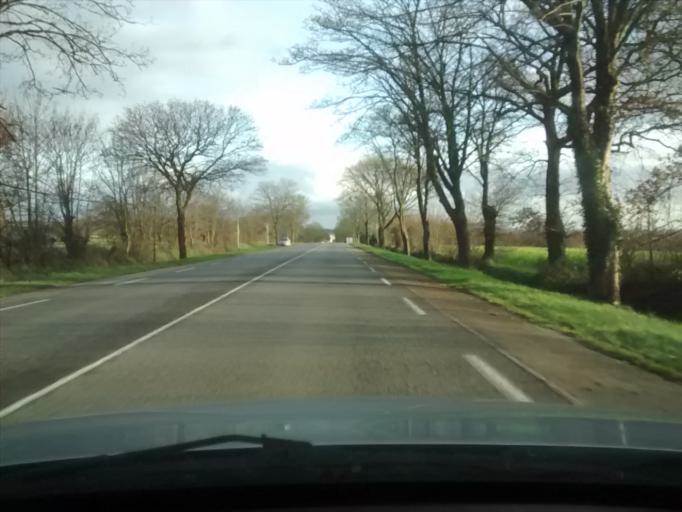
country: FR
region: Pays de la Loire
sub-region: Departement de la Mayenne
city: Saint-Pierre-la-Cour
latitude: 48.0767
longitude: -1.0258
